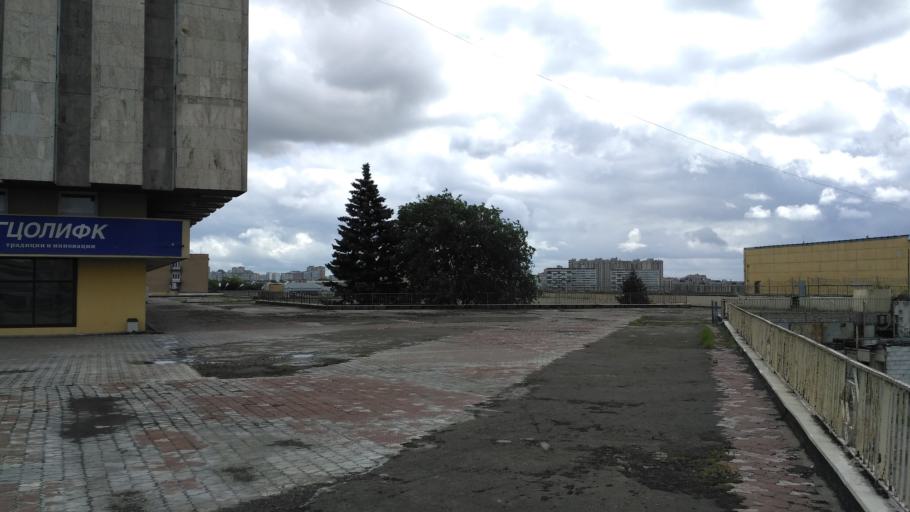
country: RU
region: Moscow
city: Metrogorodok
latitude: 55.8008
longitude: 37.7546
